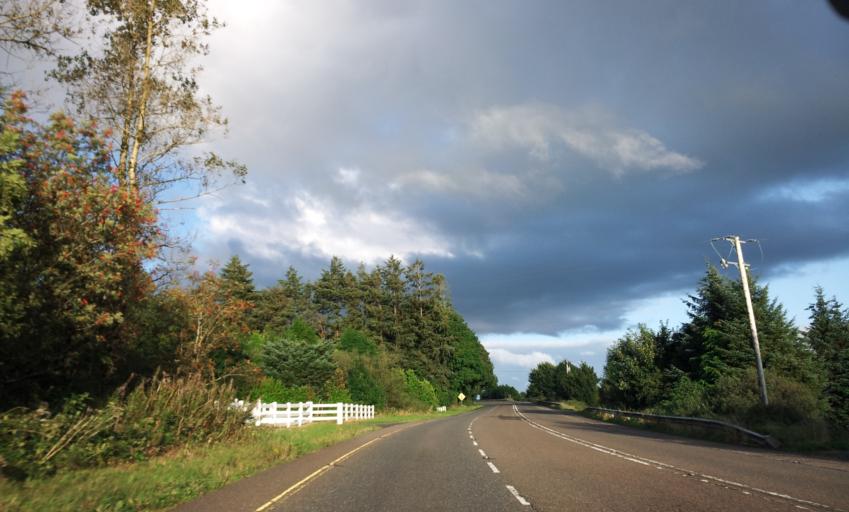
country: IE
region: Munster
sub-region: Ciarrai
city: Castleisland
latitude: 52.2659
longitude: -9.4407
